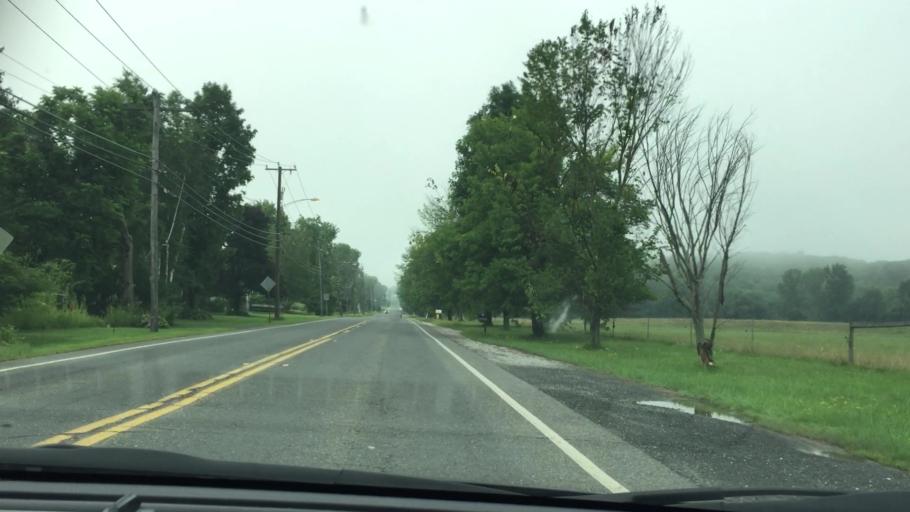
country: US
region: Massachusetts
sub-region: Berkshire County
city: Richmond
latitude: 42.4305
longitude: -73.3328
